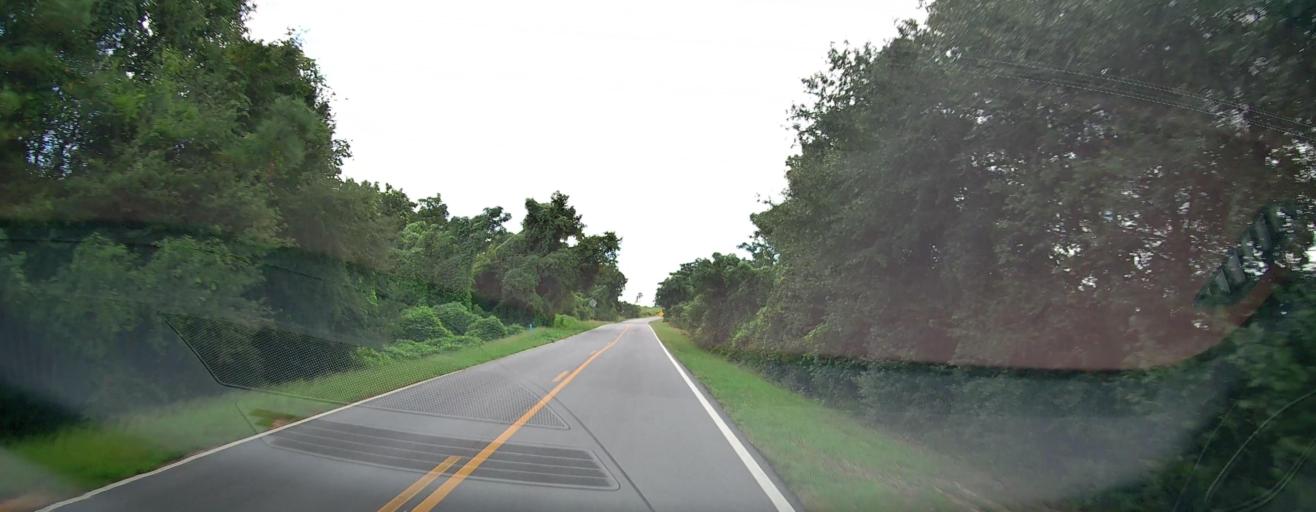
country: US
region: Georgia
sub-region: Chattahoochee County
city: Cusseta
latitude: 32.3088
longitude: -84.7448
